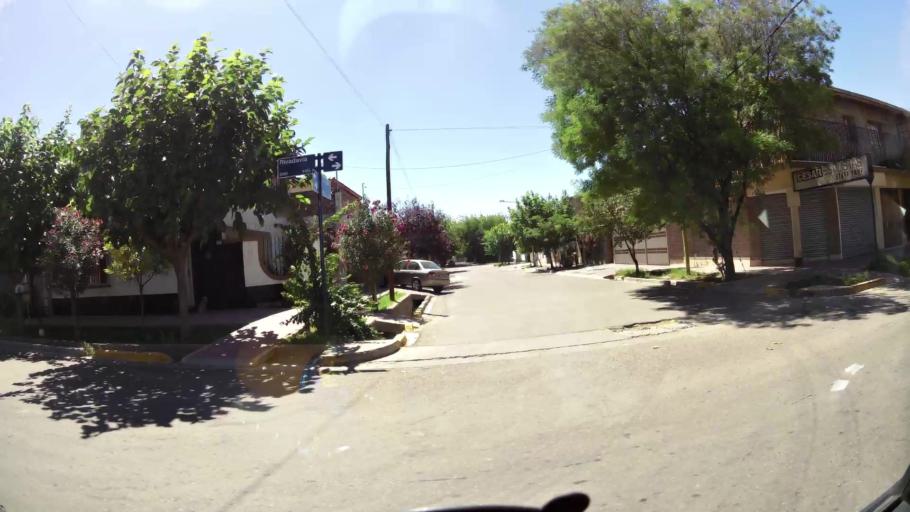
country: AR
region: Mendoza
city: Las Heras
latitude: -32.8505
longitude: -68.8473
